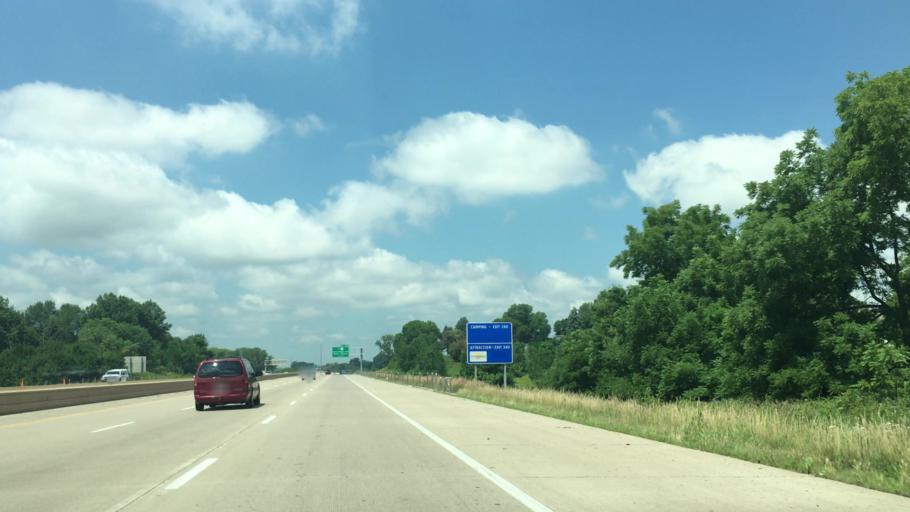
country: US
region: Iowa
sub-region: Johnson County
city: Coralville
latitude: 41.6898
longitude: -91.5841
